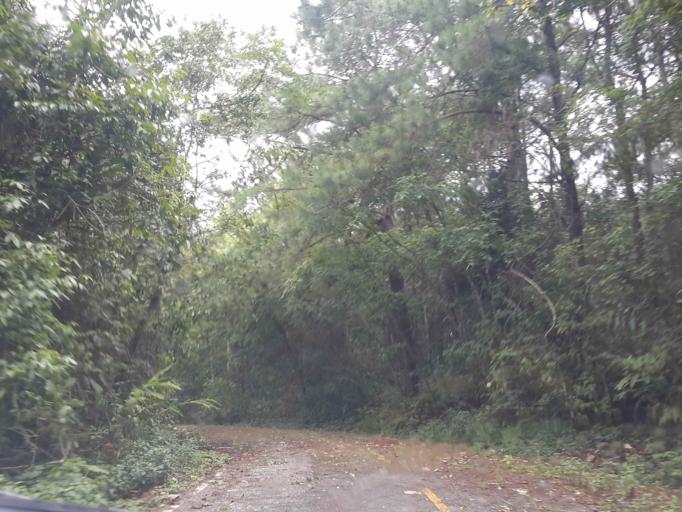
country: TH
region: Chiang Mai
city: Mae Chaem
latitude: 18.5061
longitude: 98.5291
